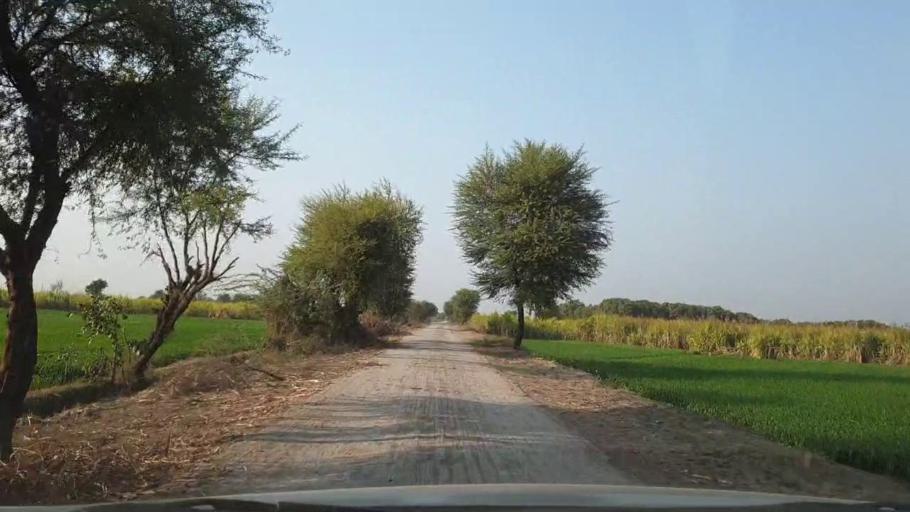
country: PK
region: Sindh
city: Tando Adam
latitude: 25.6764
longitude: 68.6359
